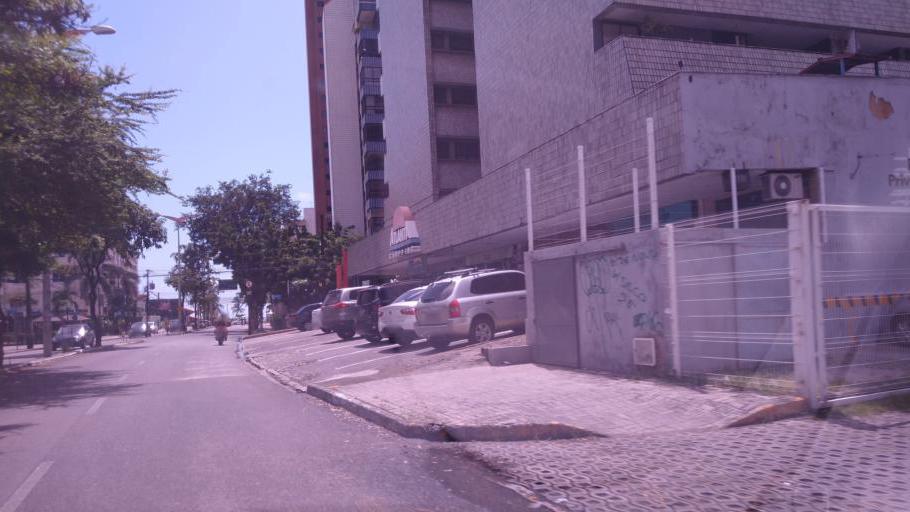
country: BR
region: Ceara
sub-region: Fortaleza
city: Fortaleza
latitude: -3.7280
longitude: -38.4910
